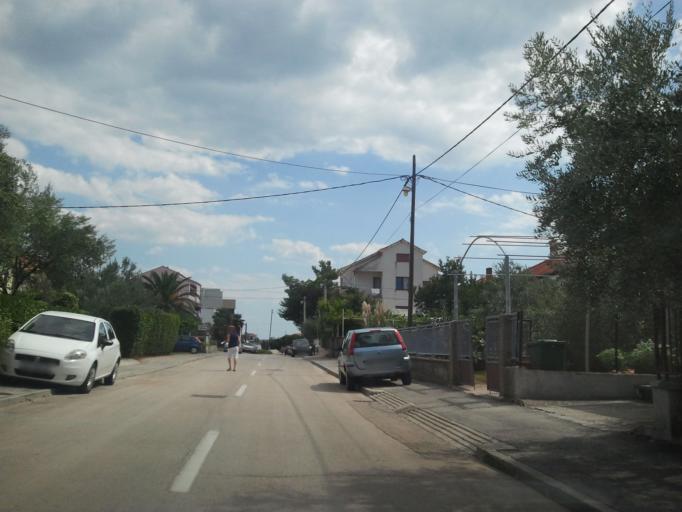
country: HR
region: Zadarska
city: Zadar
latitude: 44.1293
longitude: 15.2168
